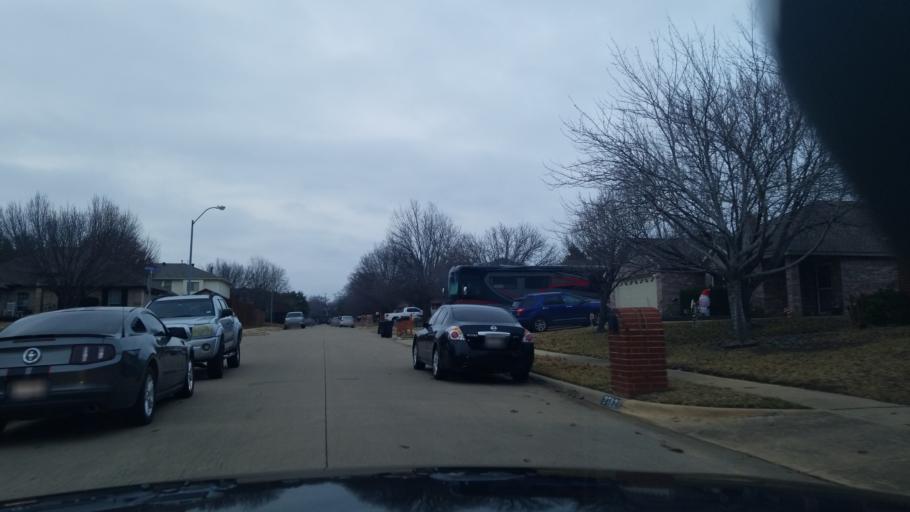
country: US
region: Texas
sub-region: Denton County
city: Corinth
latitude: 33.1390
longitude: -97.0758
